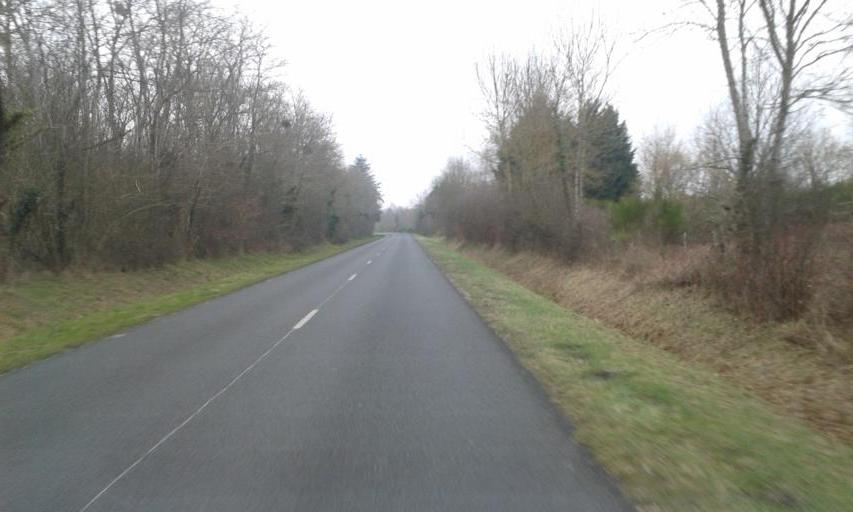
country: FR
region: Centre
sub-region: Departement du Loiret
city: Lailly-en-Val
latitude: 47.7256
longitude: 1.6556
